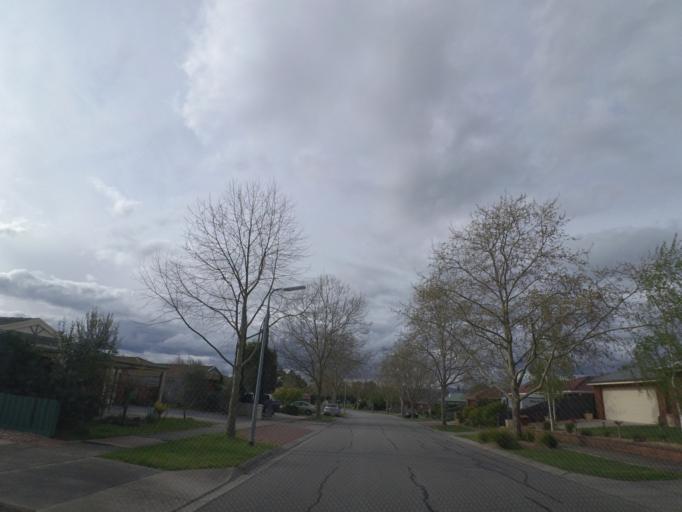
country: AU
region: Victoria
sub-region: Yarra Ranges
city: Lilydale
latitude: -37.7432
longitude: 145.3467
